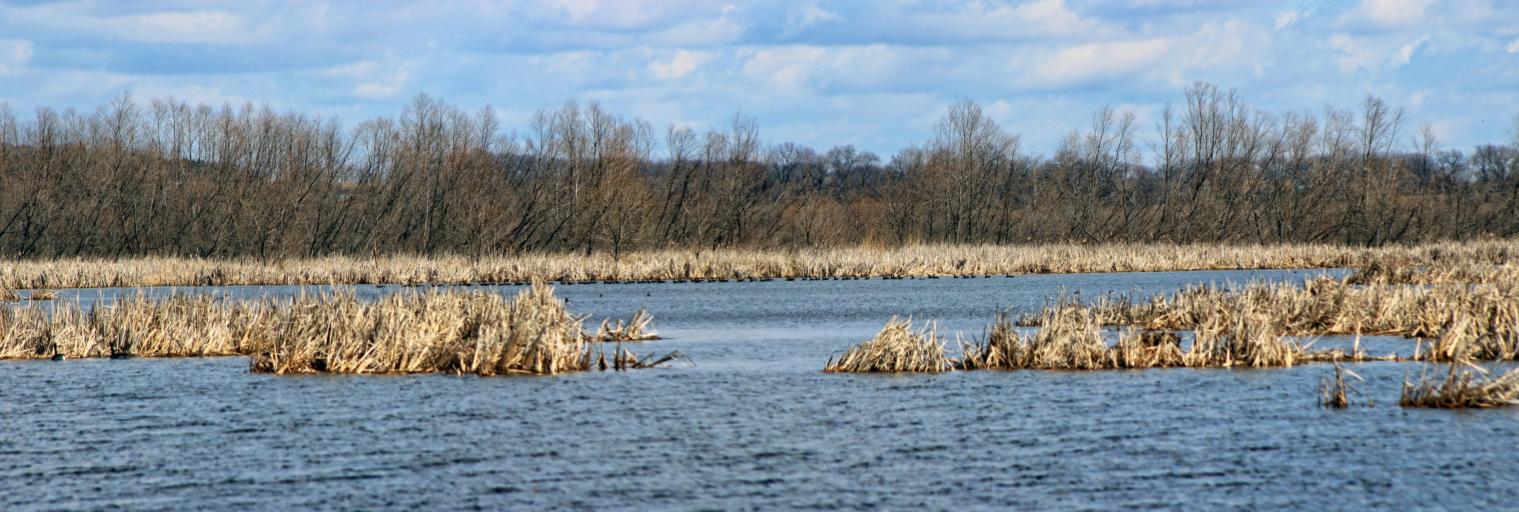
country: US
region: Wisconsin
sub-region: Jefferson County
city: Lake Ripley
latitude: 43.0392
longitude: -88.9885
